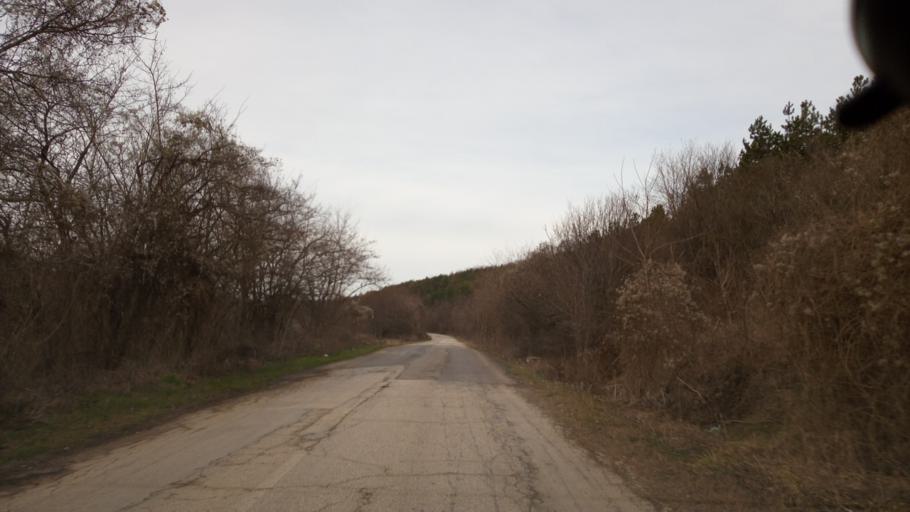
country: BG
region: Pleven
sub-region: Obshtina Nikopol
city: Nikopol
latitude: 43.5961
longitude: 24.9882
